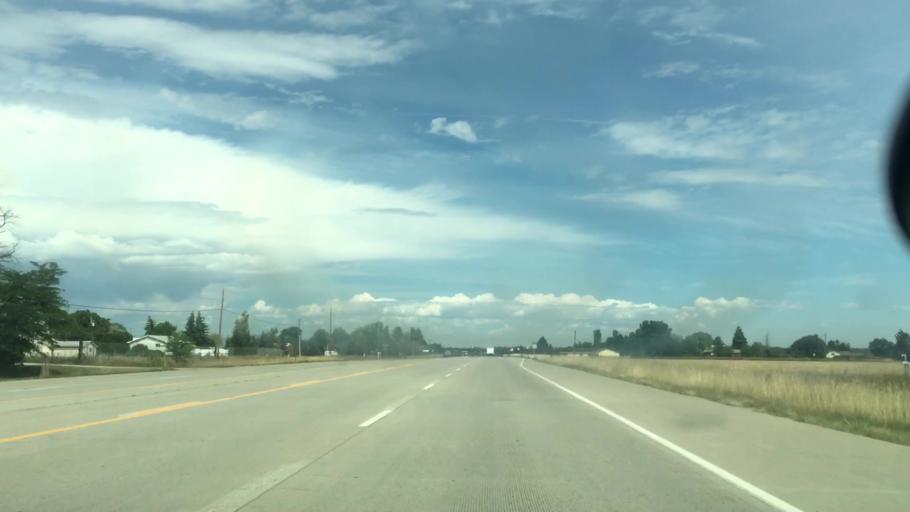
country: US
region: Colorado
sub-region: Larimer County
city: Berthoud
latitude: 40.2657
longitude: -105.1023
